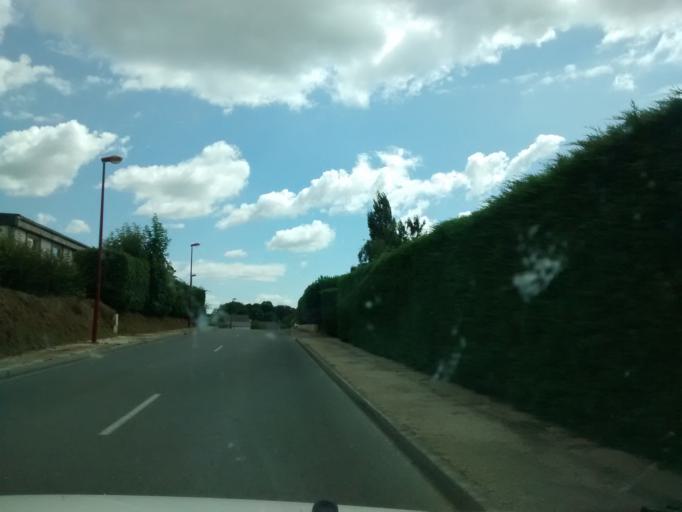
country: FR
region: Brittany
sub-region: Departement du Finistere
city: Lesneven
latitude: 48.5619
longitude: -4.2630
